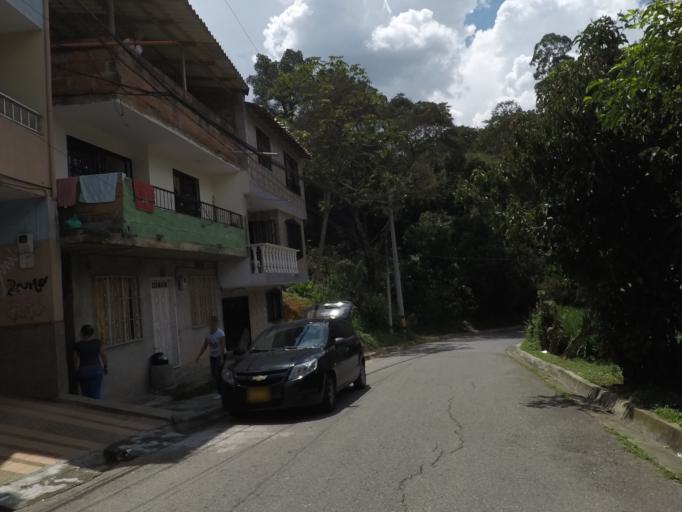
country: CO
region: Antioquia
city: Medellin
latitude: 6.2716
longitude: -75.6296
